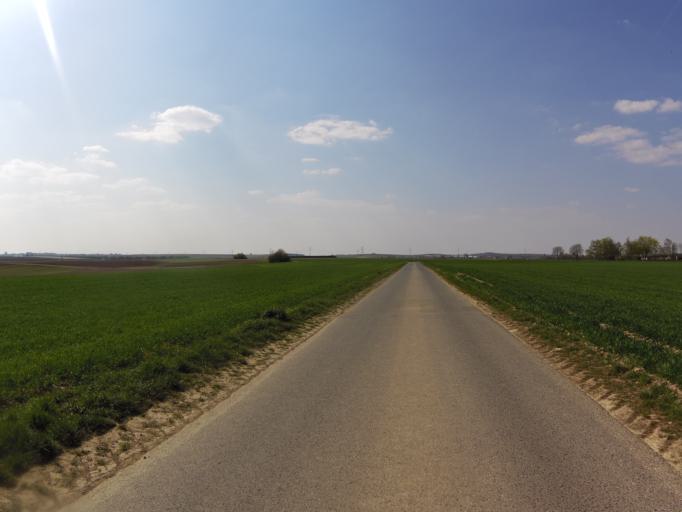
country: DE
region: Bavaria
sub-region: Regierungsbezirk Unterfranken
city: Mainstockheim
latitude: 49.8163
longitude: 10.1273
